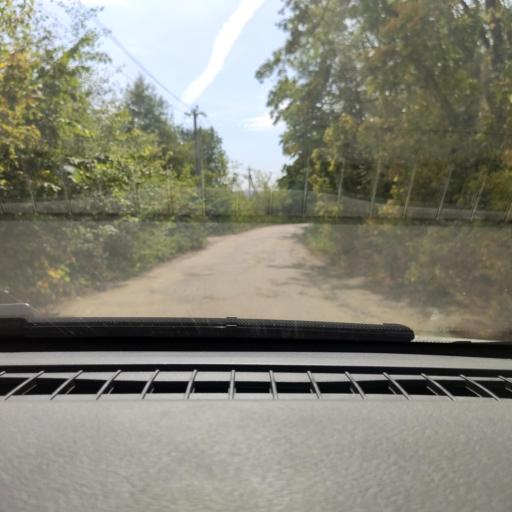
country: RU
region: Voronezj
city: Pridonskoy
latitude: 51.7544
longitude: 39.0787
